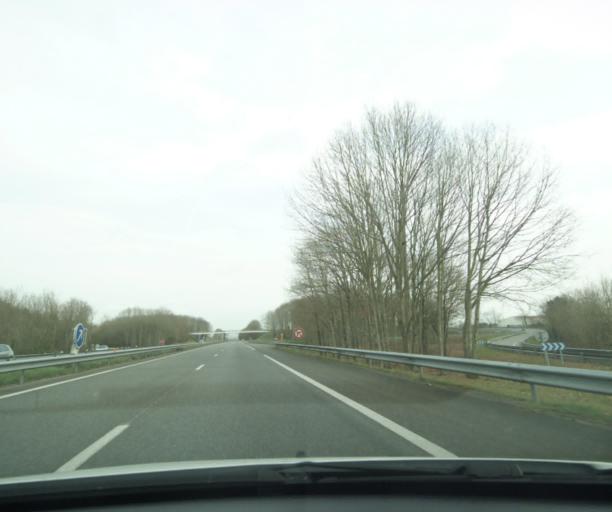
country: FR
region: Aquitaine
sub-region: Departement des Landes
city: Peyrehorade
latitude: 43.5140
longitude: -1.1074
